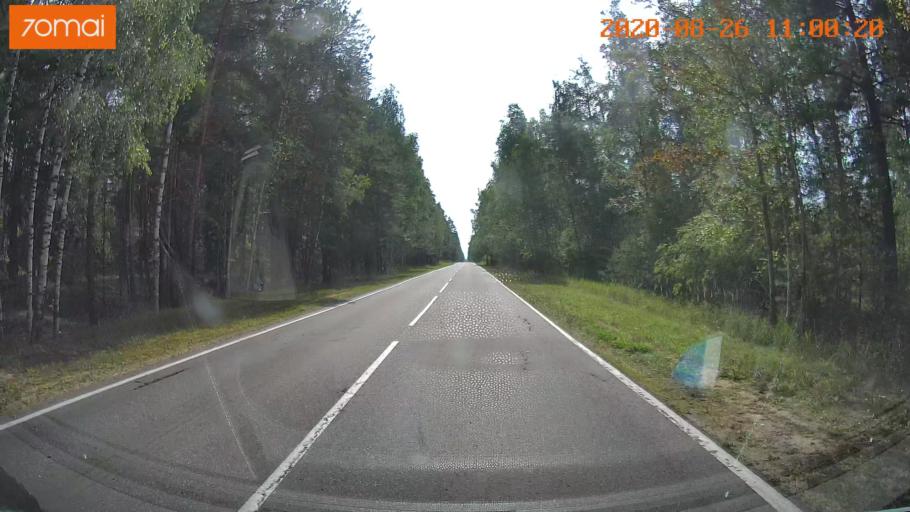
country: RU
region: Rjazan
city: Izhevskoye
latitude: 54.5758
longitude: 41.2122
